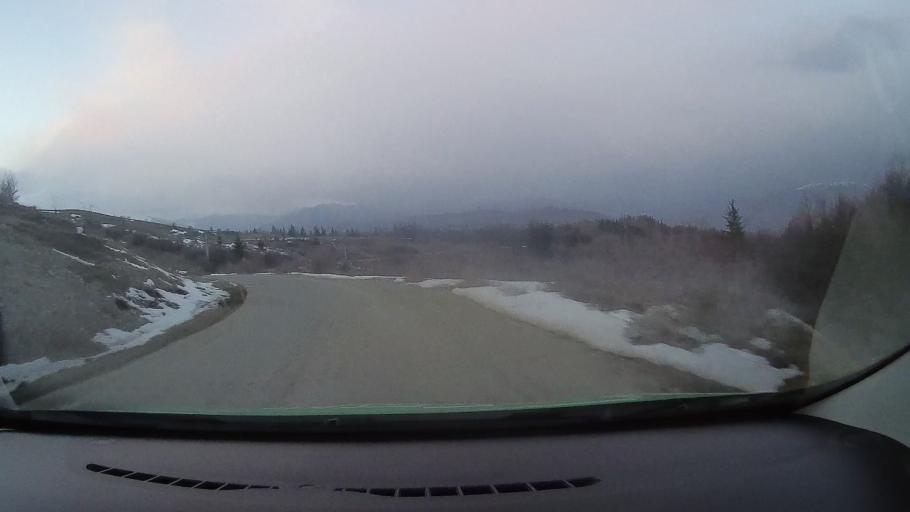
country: RO
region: Prahova
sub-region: Comuna Secaria
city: Secaria
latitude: 45.2849
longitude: 25.7023
